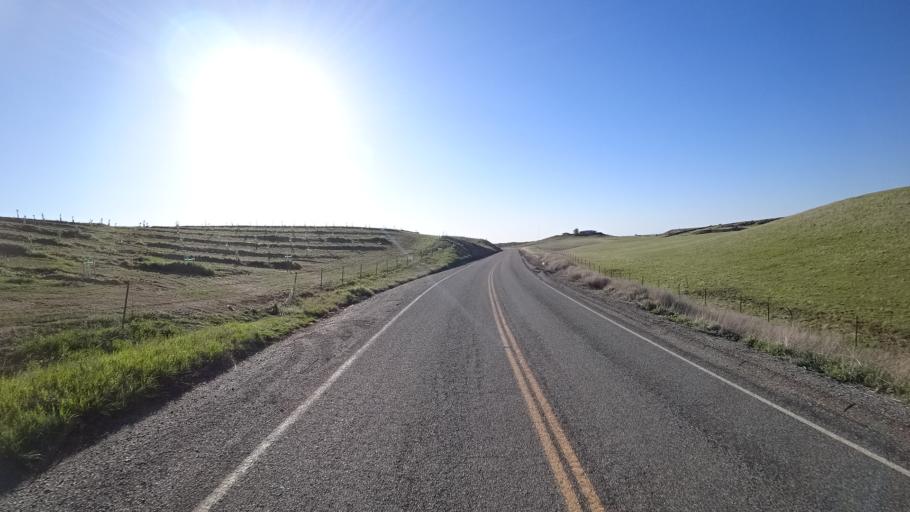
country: US
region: California
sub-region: Glenn County
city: Orland
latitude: 39.8311
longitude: -122.3412
